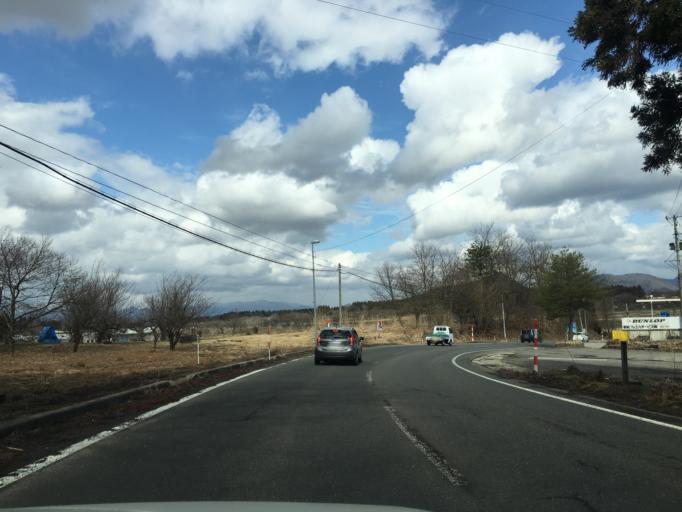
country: JP
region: Akita
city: Odate
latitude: 40.2034
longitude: 140.5554
